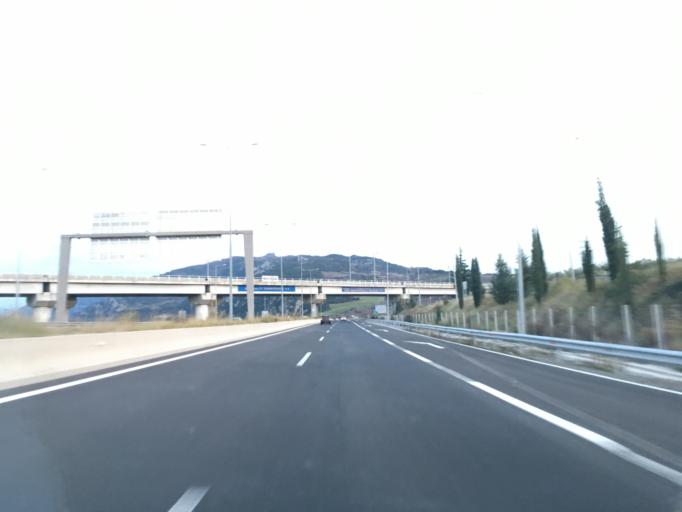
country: GR
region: Central Greece
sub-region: Nomos Fthiotidos
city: Kainouryion
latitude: 38.7854
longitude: 22.7012
